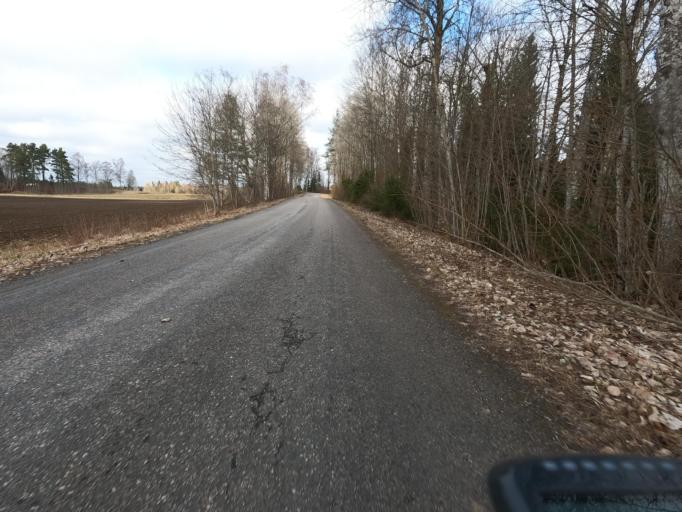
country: SE
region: Kronoberg
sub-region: Alvesta Kommun
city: Vislanda
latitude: 56.8116
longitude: 14.4957
